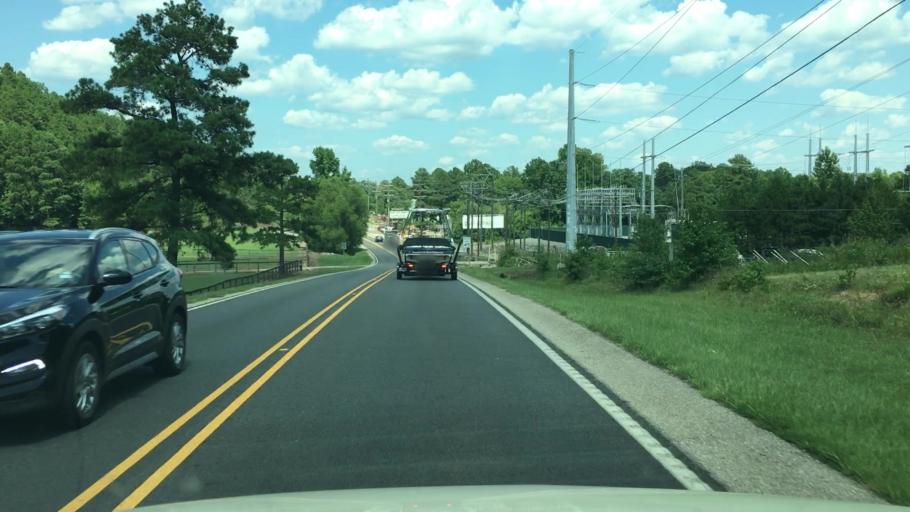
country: US
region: Arkansas
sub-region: Garland County
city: Lake Hamilton
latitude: 34.4027
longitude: -93.0943
